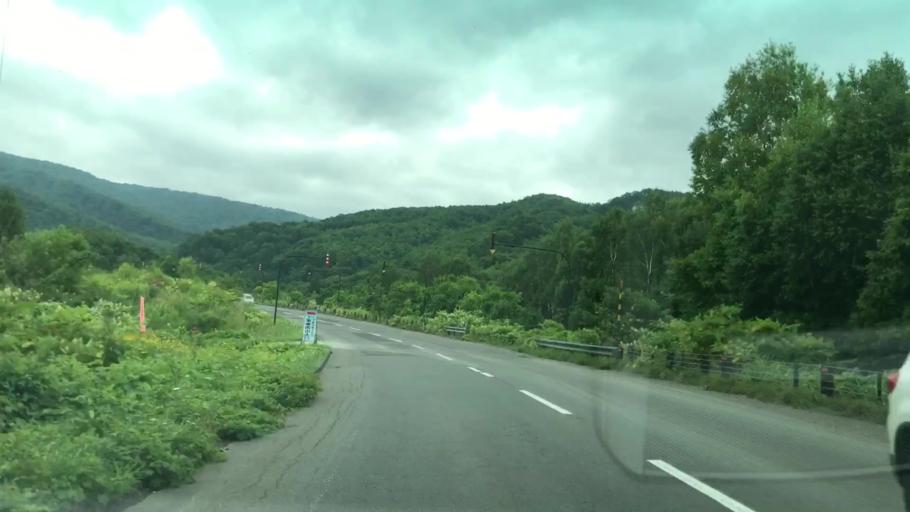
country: JP
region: Hokkaido
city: Yoichi
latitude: 43.0114
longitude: 140.8689
